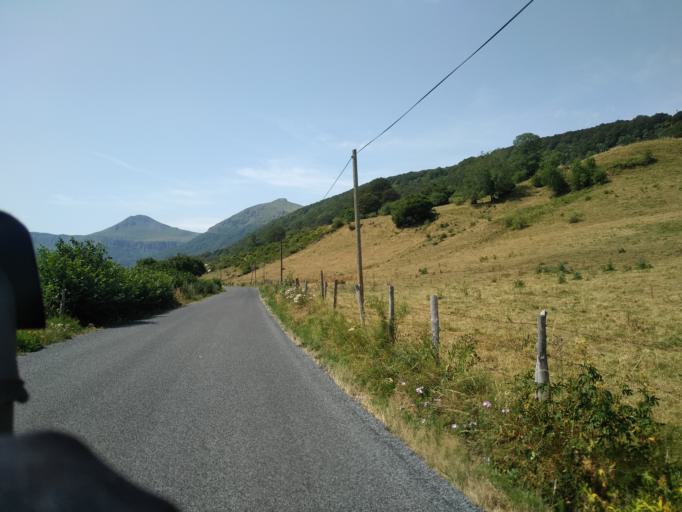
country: FR
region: Auvergne
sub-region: Departement du Cantal
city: Riom-es-Montagnes
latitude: 45.1522
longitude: 2.7008
